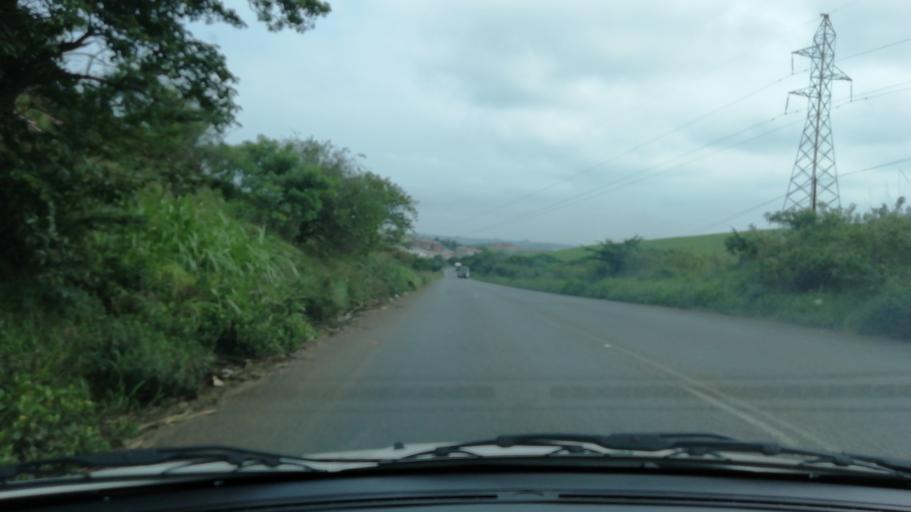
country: ZA
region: KwaZulu-Natal
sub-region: uThungulu District Municipality
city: Empangeni
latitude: -28.7442
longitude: 31.8808
